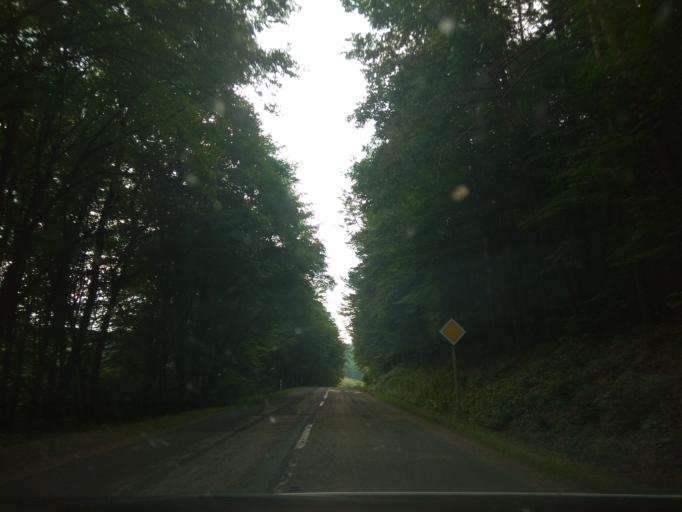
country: HU
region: Heves
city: Tarnalelesz
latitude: 48.0558
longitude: 20.2292
